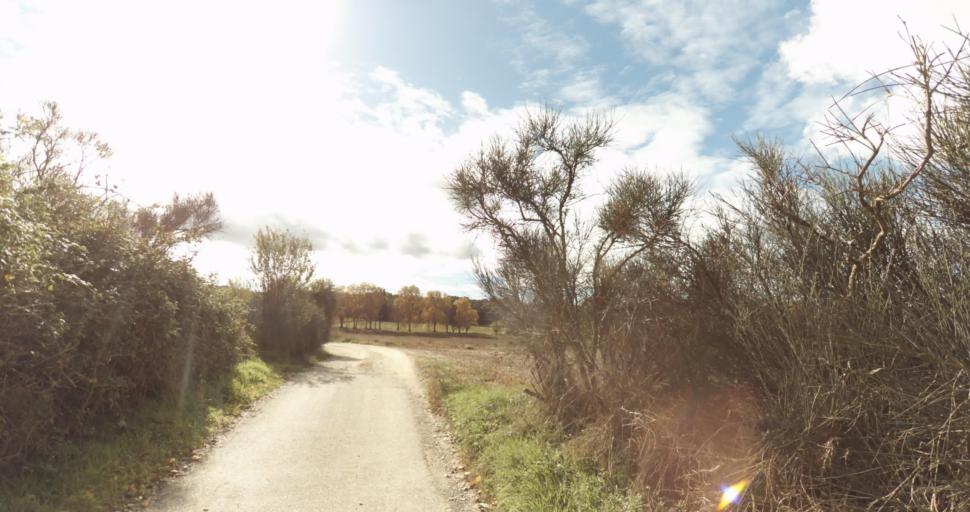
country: FR
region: Provence-Alpes-Cote d'Azur
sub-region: Departement des Bouches-du-Rhone
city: Venelles
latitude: 43.5834
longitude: 5.4843
